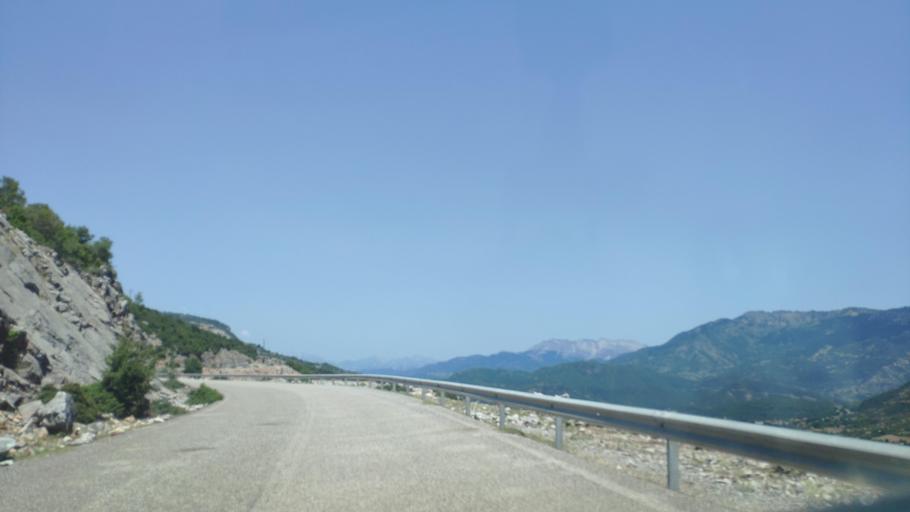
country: GR
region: Thessaly
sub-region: Nomos Kardhitsas
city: Anthiro
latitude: 39.1261
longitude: 21.3984
